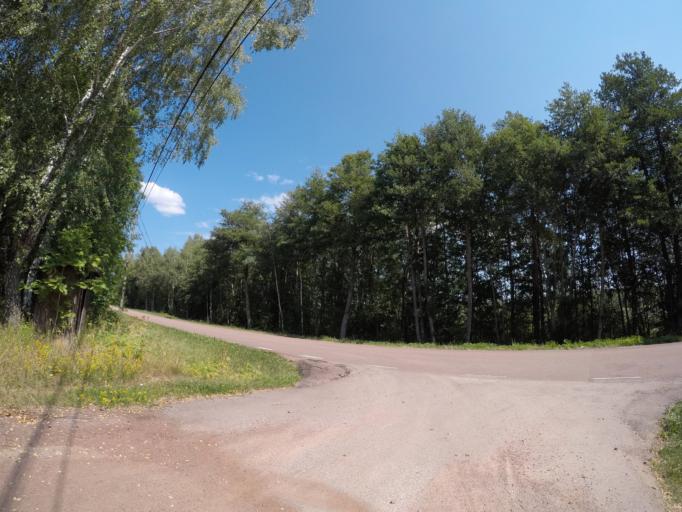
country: AX
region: Alands landsbygd
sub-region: Finstroem
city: Finstroem
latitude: 60.2189
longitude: 19.8607
